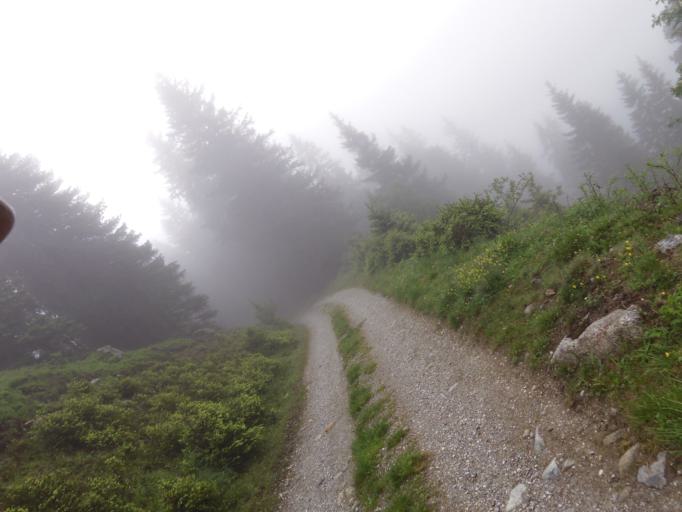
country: AT
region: Tyrol
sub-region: Politischer Bezirk Innsbruck Land
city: Neustift im Stubaital
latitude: 47.0521
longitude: 11.2215
